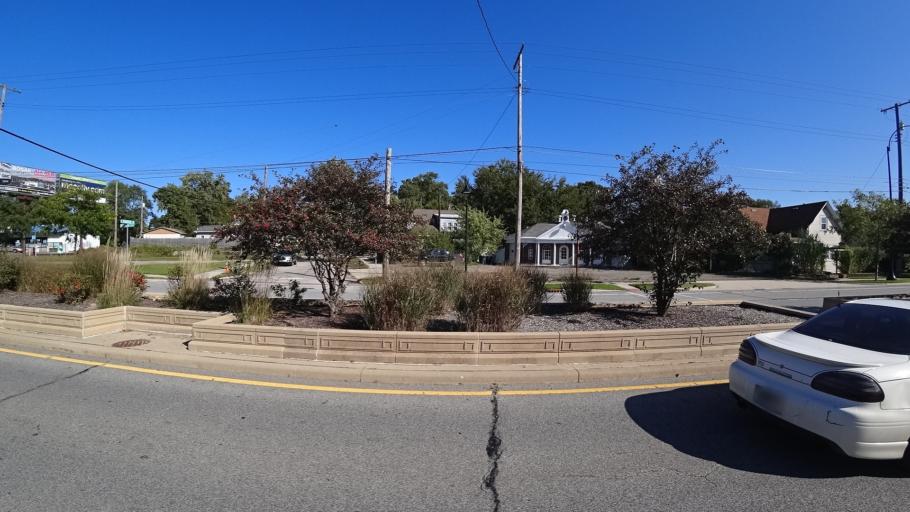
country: US
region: Indiana
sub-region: LaPorte County
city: Michigan City
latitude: 41.7114
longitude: -86.8809
